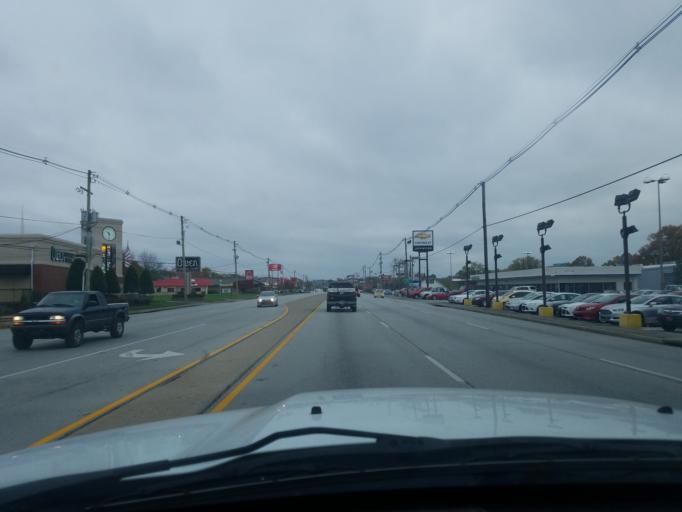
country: US
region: Kentucky
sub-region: Jefferson County
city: Pleasure Ridge Park
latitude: 38.1598
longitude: -85.8329
